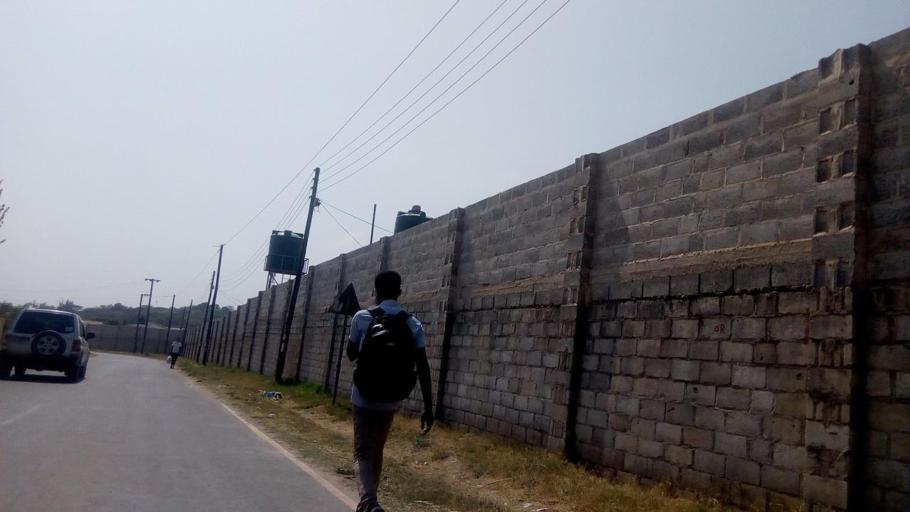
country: ZM
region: Lusaka
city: Lusaka
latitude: -15.3622
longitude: 28.2860
